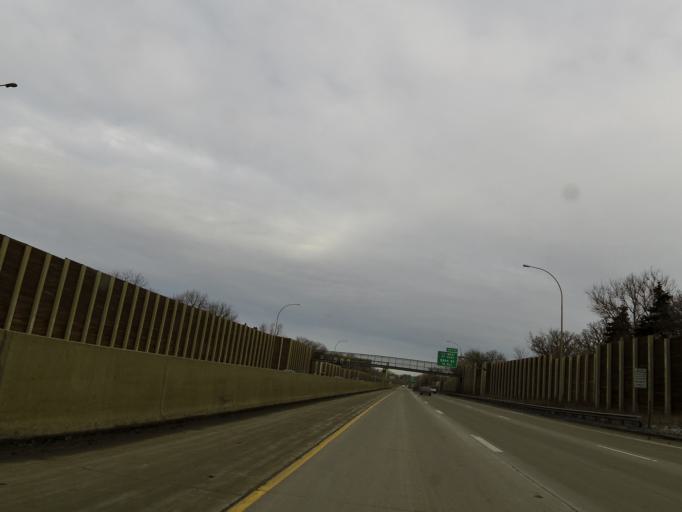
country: US
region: Minnesota
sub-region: Hennepin County
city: Richfield
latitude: 44.8696
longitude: -93.2989
